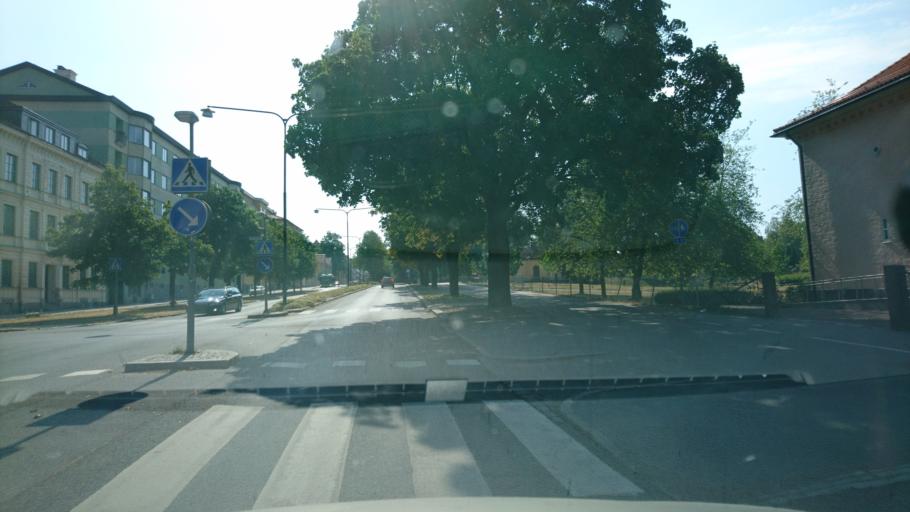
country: SE
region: Uppsala
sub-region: Uppsala Kommun
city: Uppsala
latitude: 59.8586
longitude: 17.6235
